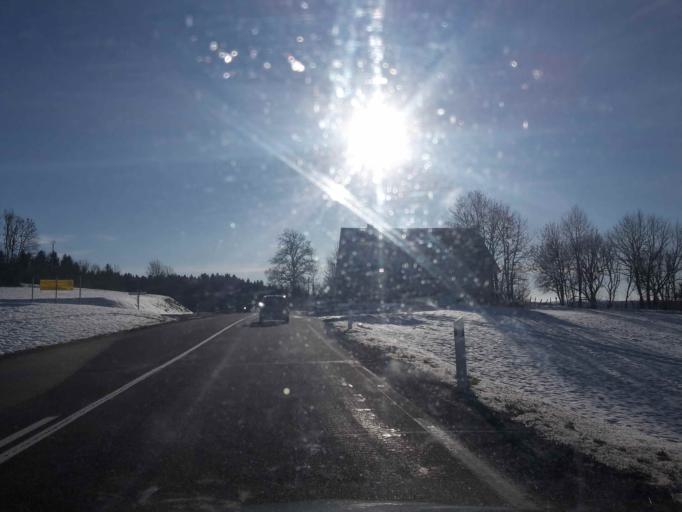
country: FR
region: Franche-Comte
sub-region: Departement du Doubs
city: Doubs
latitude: 47.0338
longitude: 6.3356
